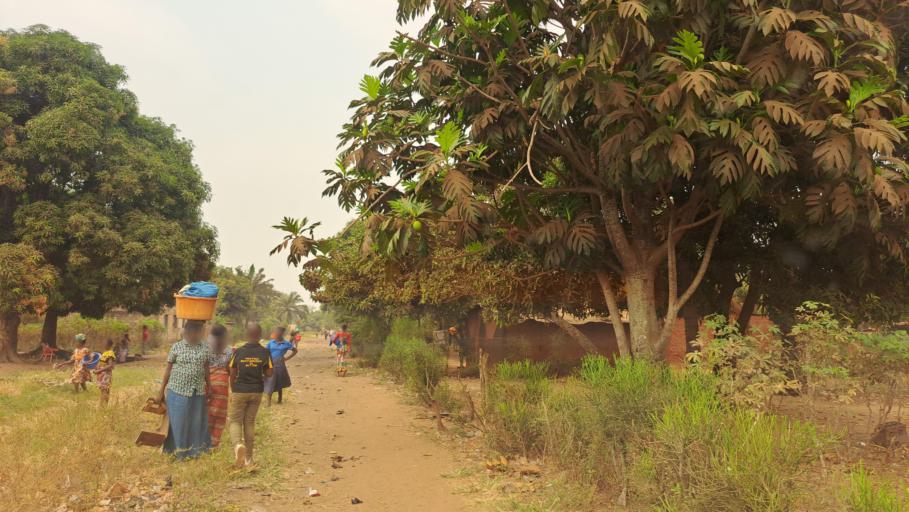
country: CD
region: Kasai-Oriental
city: Mbuji-Mayi
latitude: -6.1222
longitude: 23.6034
